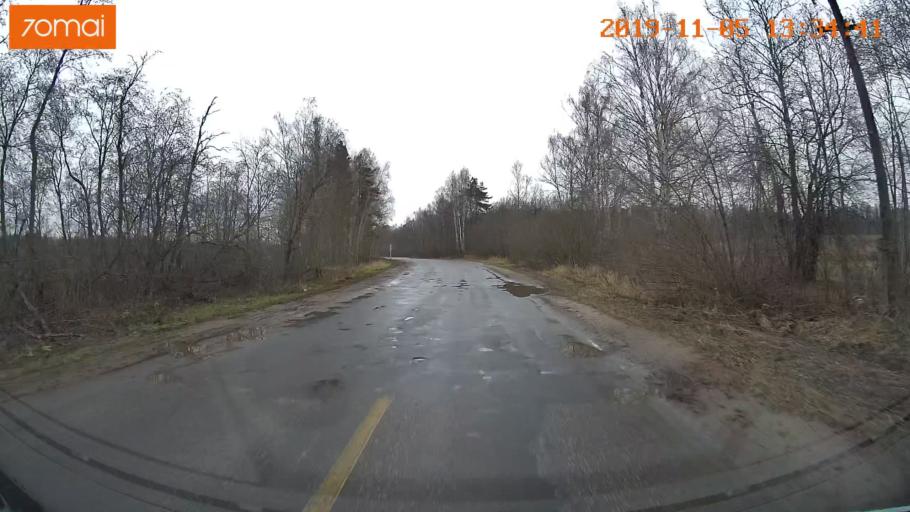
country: RU
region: Ivanovo
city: Shuya
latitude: 56.9026
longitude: 41.3899
